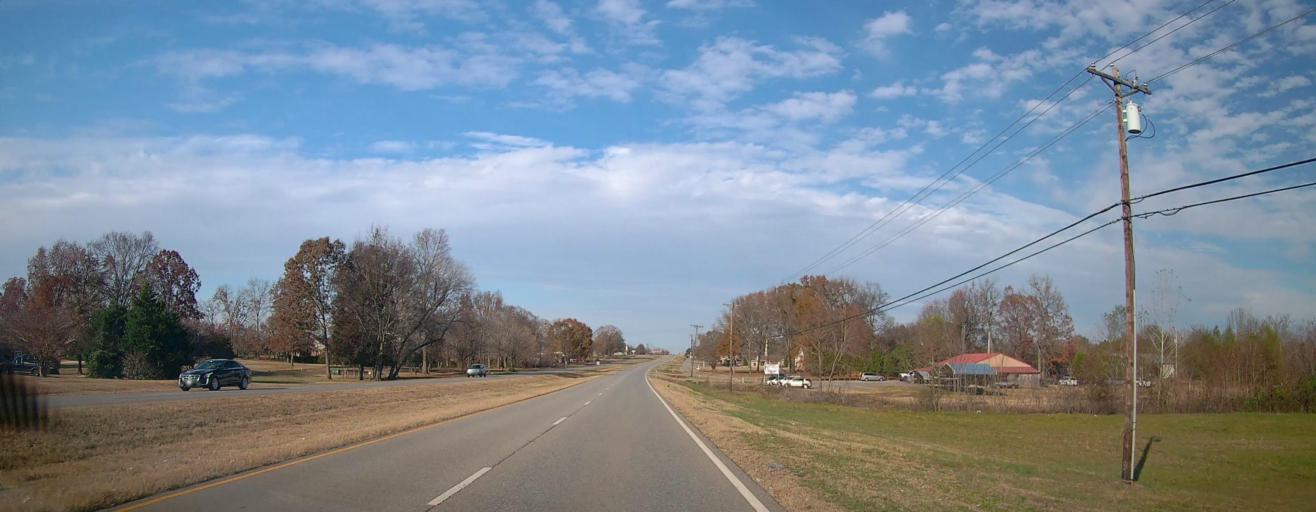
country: US
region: Alabama
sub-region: Limestone County
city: Athens
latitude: 34.7223
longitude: -86.9568
